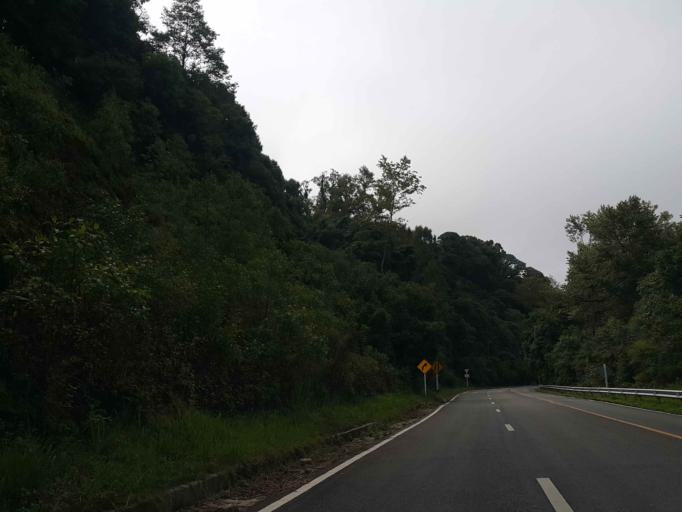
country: TH
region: Chiang Mai
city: Mae Chaem
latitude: 18.5598
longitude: 98.4834
